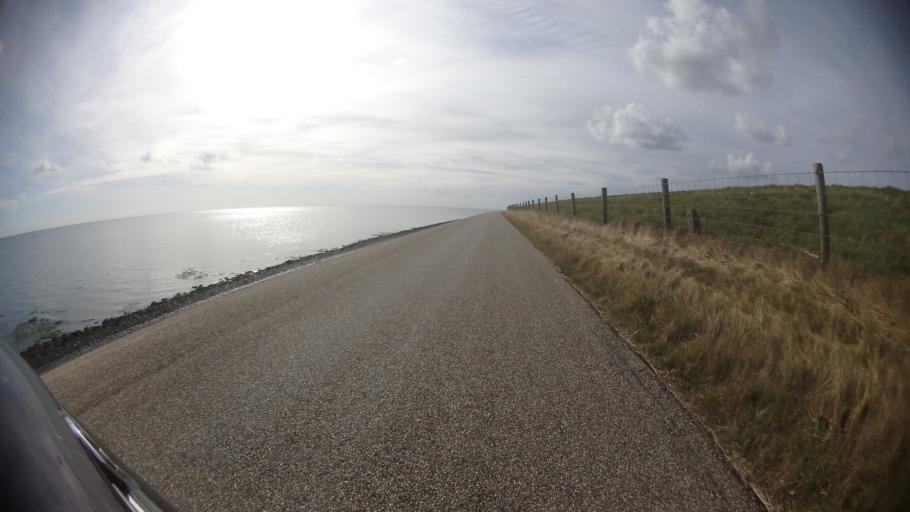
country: NL
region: North Holland
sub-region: Gemeente Texel
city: Den Burg
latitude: 53.0863
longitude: 4.9001
